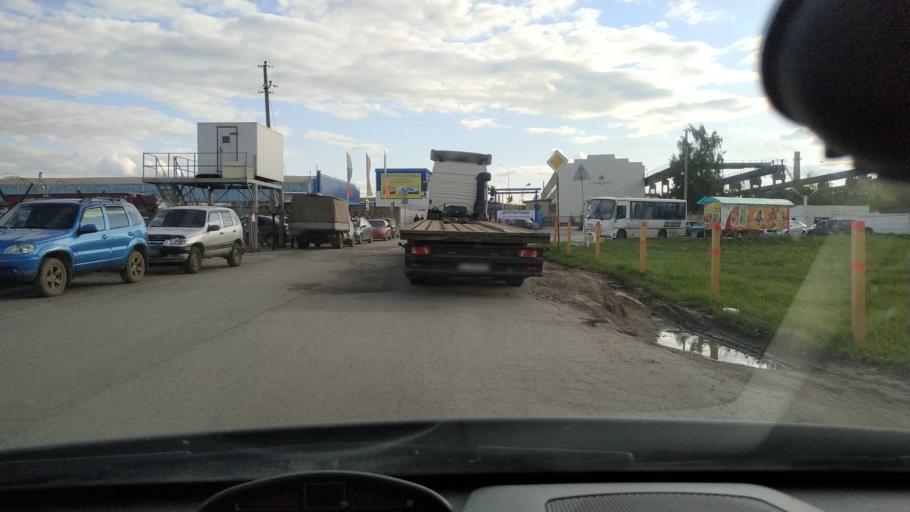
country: RU
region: Rjazan
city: Polyany
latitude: 54.5794
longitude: 39.8384
